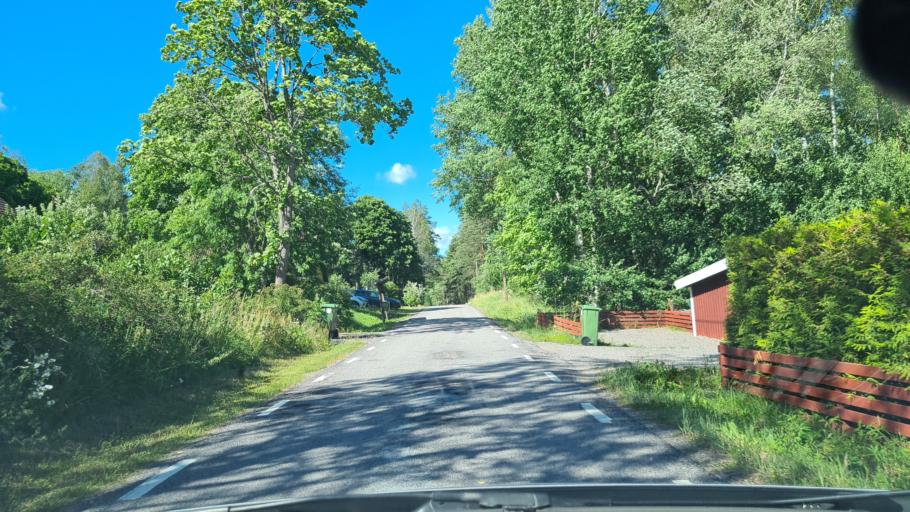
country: SE
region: OEstergoetland
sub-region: Norrkopings Kommun
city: Krokek
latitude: 58.7182
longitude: 16.4296
